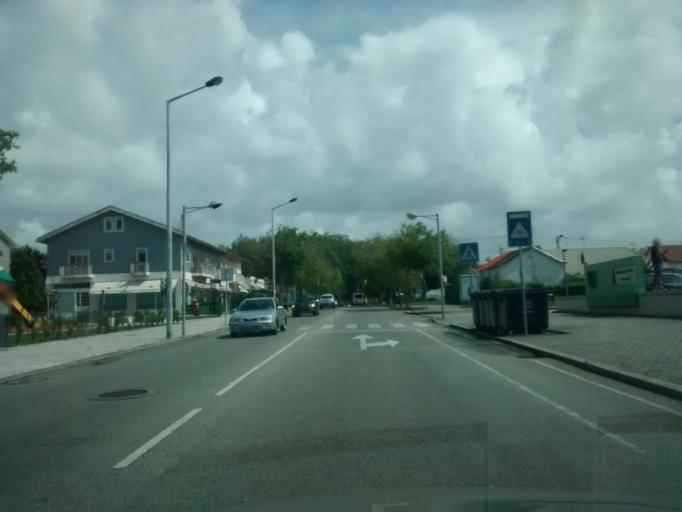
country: PT
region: Aveiro
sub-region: Aveiro
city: Aveiro
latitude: 40.6368
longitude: -8.6570
